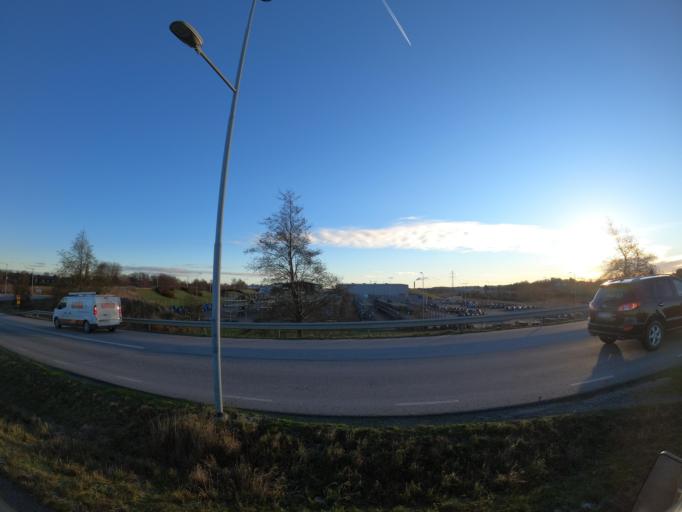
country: SE
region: Skane
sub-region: Svedala Kommun
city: Svedala
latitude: 55.5089
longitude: 13.2158
